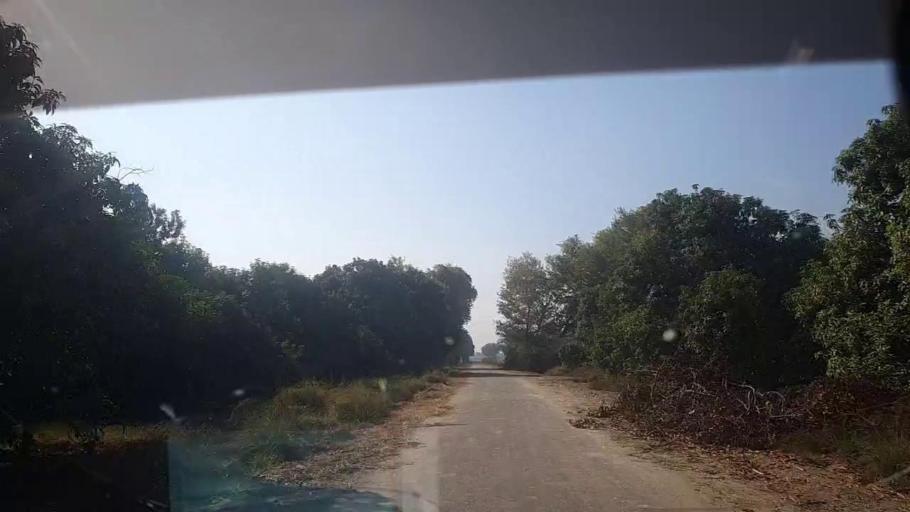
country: PK
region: Sindh
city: Gambat
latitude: 27.3873
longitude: 68.5978
